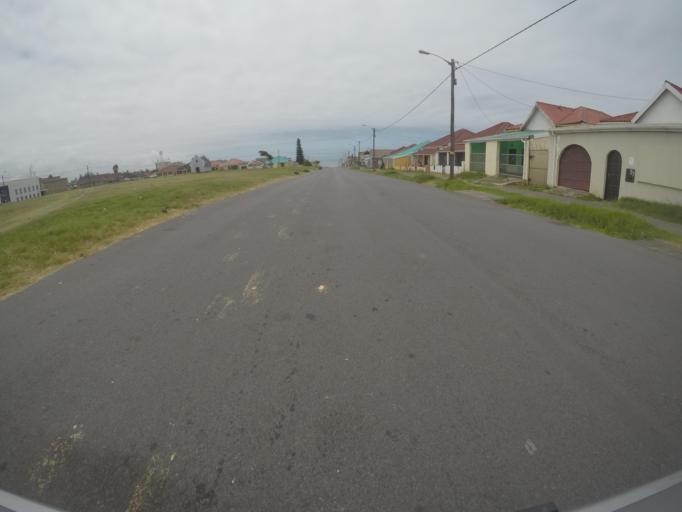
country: ZA
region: Eastern Cape
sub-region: Buffalo City Metropolitan Municipality
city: East London
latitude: -33.0151
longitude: 27.9146
